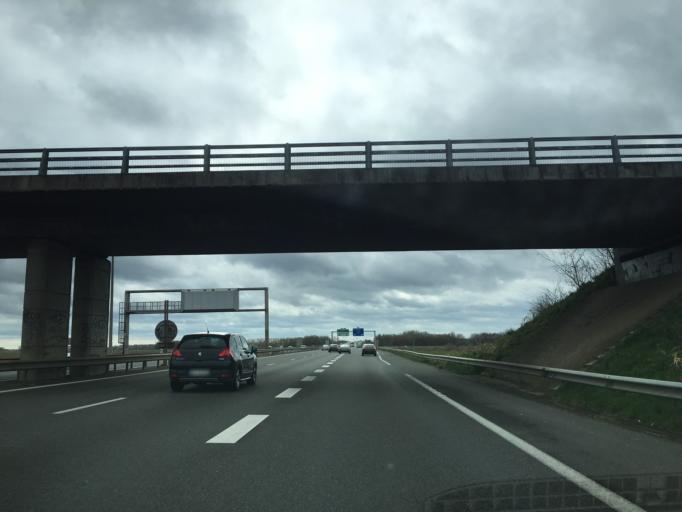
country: FR
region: Ile-de-France
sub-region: Departement de Seine-et-Marne
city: Vert-Saint-Denis
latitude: 48.6019
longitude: 2.6340
